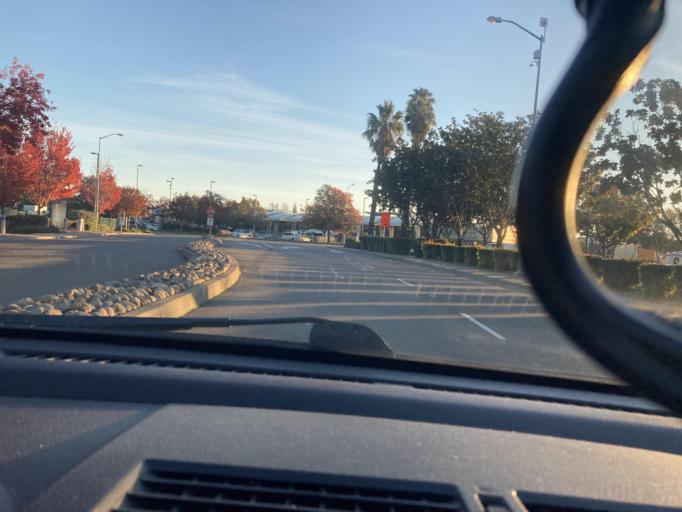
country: US
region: California
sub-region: Solano County
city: Fairfield
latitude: 38.2481
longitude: -122.0699
